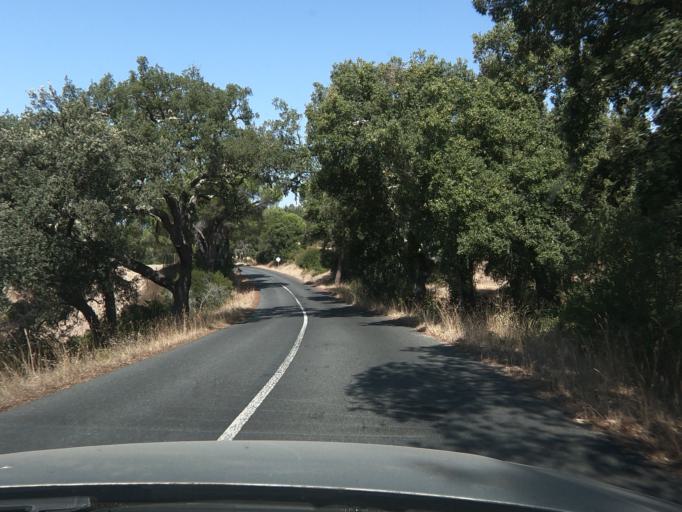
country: PT
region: Setubal
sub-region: Alcacer do Sal
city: Alcacer do Sal
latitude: 38.3001
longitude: -8.4045
